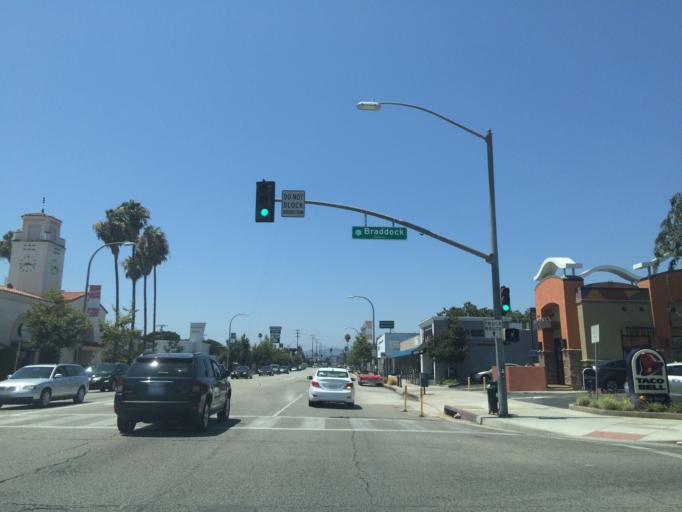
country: US
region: California
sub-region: Los Angeles County
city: Culver City
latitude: 34.0029
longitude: -118.4067
